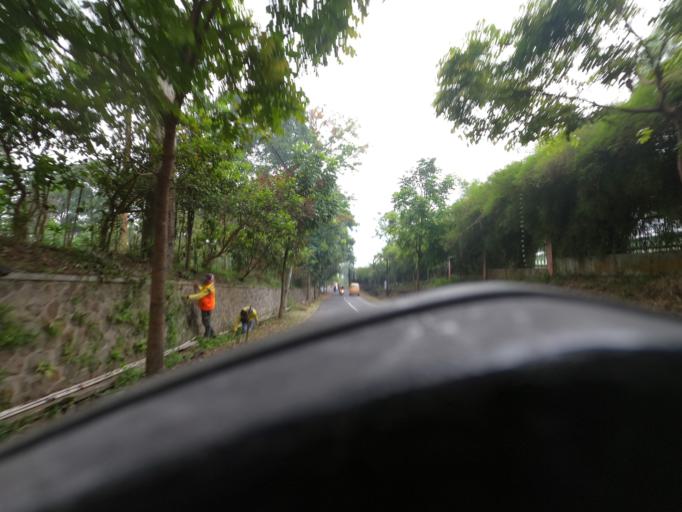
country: ID
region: West Java
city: Lembang
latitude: -6.8021
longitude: 107.5709
